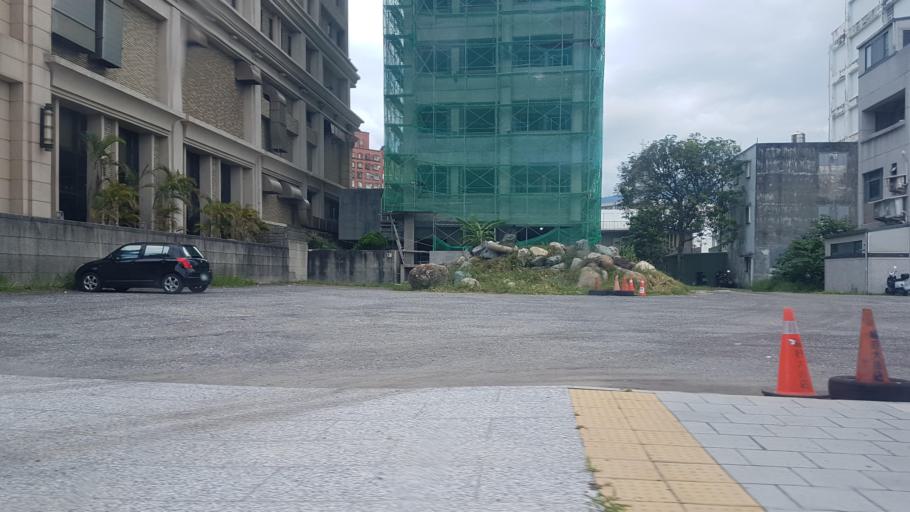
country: TW
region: Taiwan
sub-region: Hualien
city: Hualian
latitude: 23.9959
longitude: 121.6333
